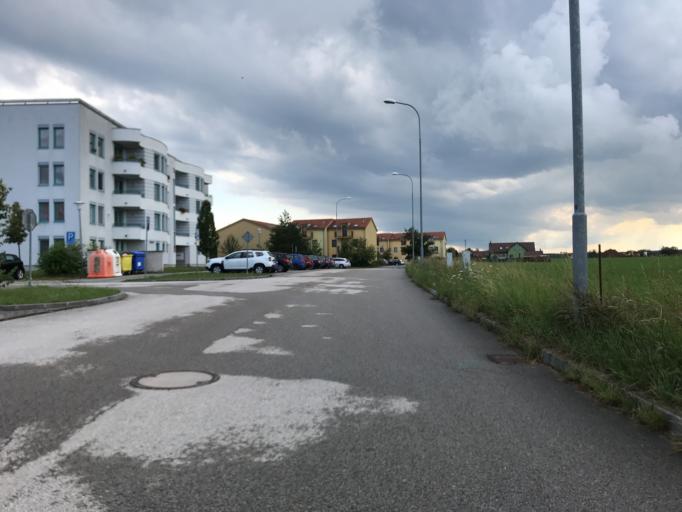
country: CZ
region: Jihocesky
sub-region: Okres Jindrichuv Hradec
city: Trebon
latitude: 49.0120
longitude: 14.7542
